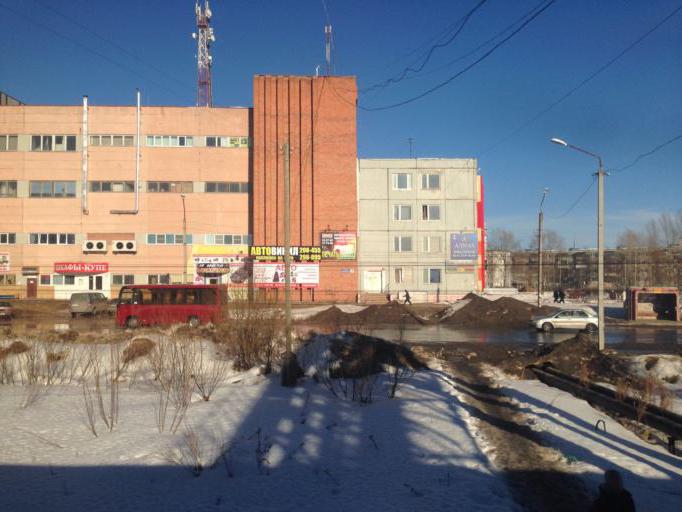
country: RU
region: Komi Republic
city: Ezhva
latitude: 61.7985
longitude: 50.7359
